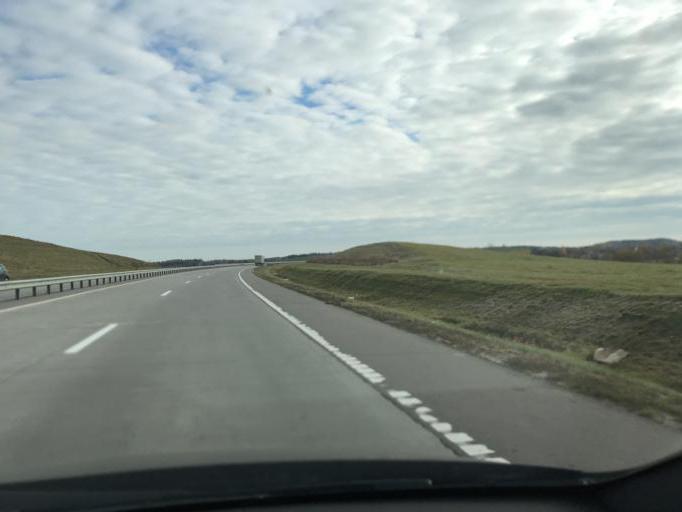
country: BY
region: Minsk
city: Pyatryshki
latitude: 54.0718
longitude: 27.2655
